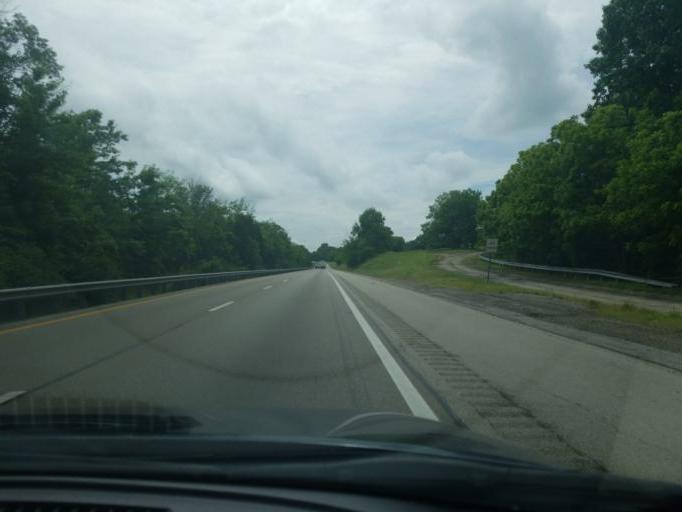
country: US
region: Indiana
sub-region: Switzerland County
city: Vevay
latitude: 38.6760
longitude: -85.0003
